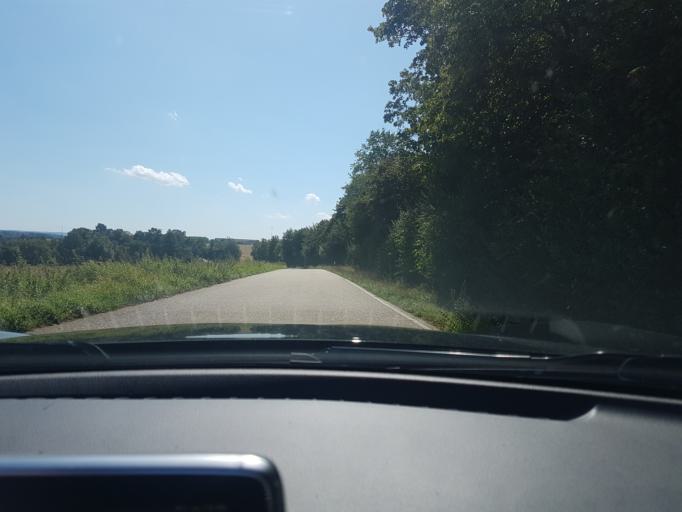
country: DE
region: Baden-Wuerttemberg
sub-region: Regierungsbezirk Stuttgart
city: Gundelsheim
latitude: 49.2709
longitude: 9.1351
